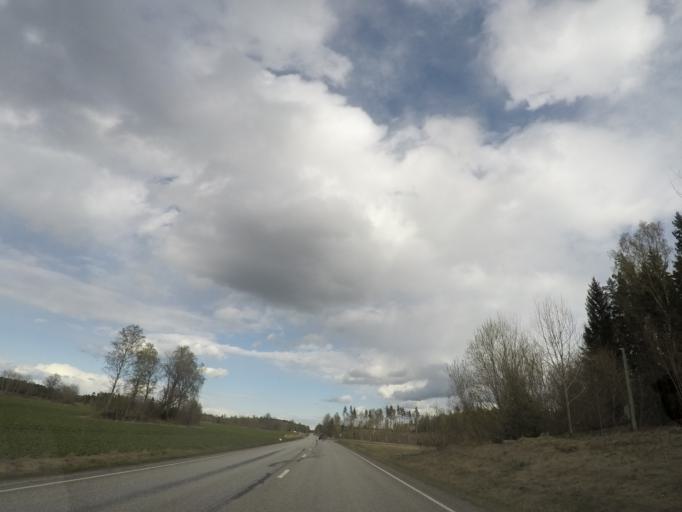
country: SE
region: Soedermanland
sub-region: Eskilstuna Kommun
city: Hallbybrunn
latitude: 59.3203
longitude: 16.3272
